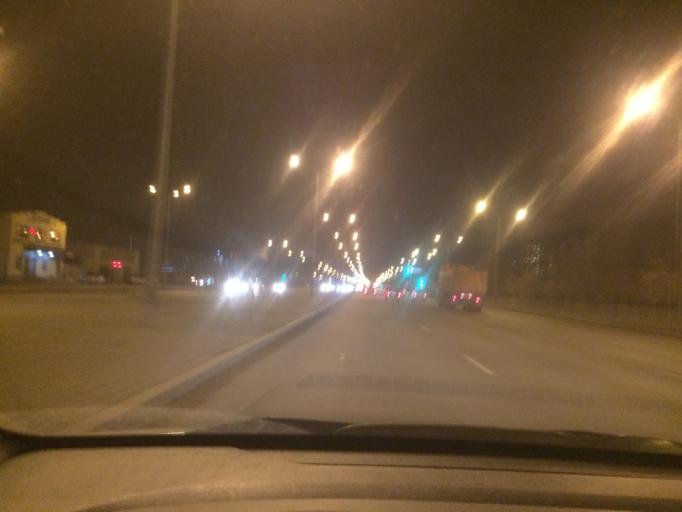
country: KZ
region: Astana Qalasy
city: Astana
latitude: 51.1833
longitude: 71.3667
